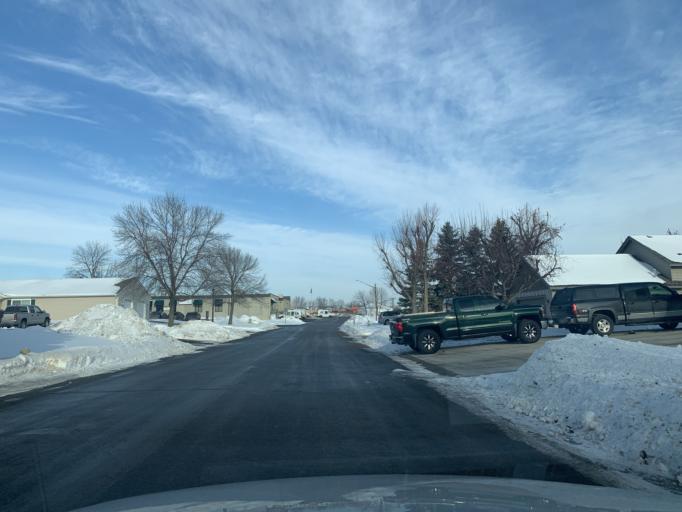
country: US
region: Minnesota
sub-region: Wright County
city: Saint Michael
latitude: 45.2080
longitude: -93.6552
